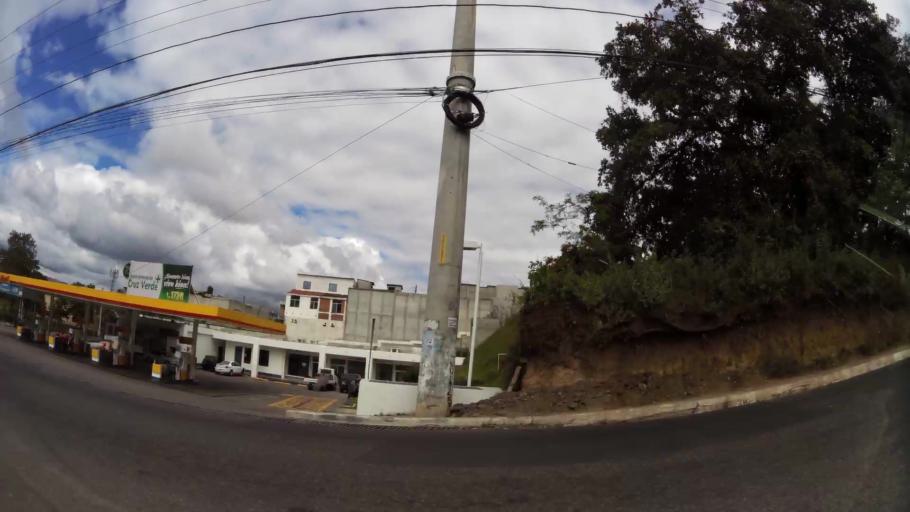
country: GT
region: Guatemala
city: Guatemala City
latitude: 14.6727
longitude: -90.5543
